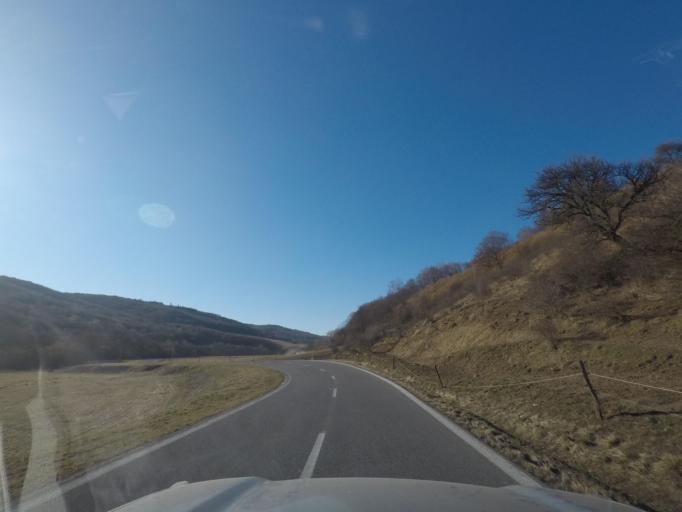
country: SK
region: Presovsky
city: Medzilaborce
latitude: 49.1792
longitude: 22.0212
